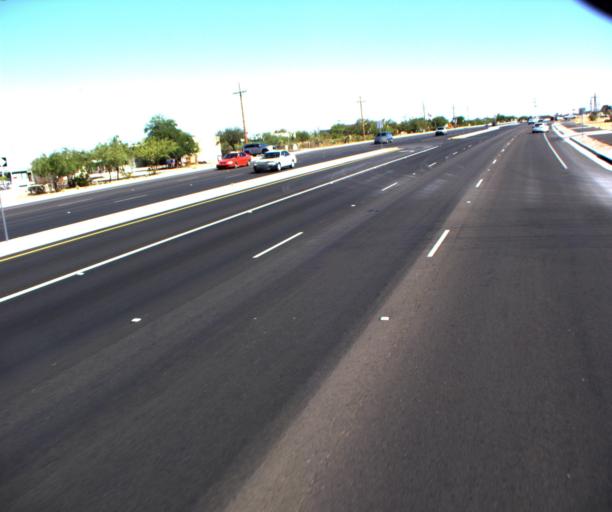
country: US
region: Arizona
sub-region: Pima County
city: Catalina
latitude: 32.4917
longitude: -110.9249
